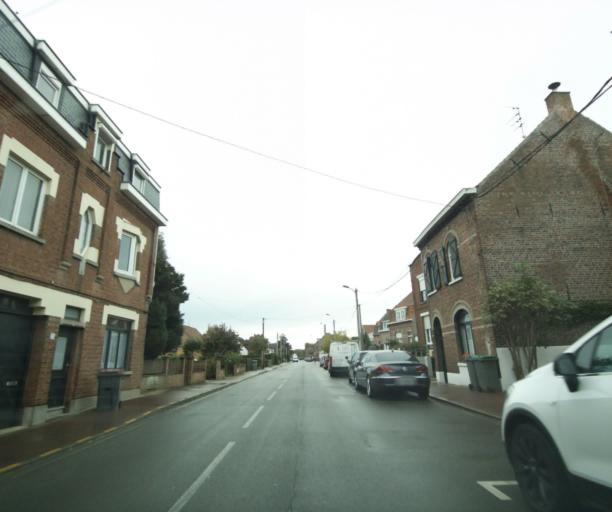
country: FR
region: Nord-Pas-de-Calais
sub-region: Departement du Nord
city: Roncq
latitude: 50.7357
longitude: 3.1267
